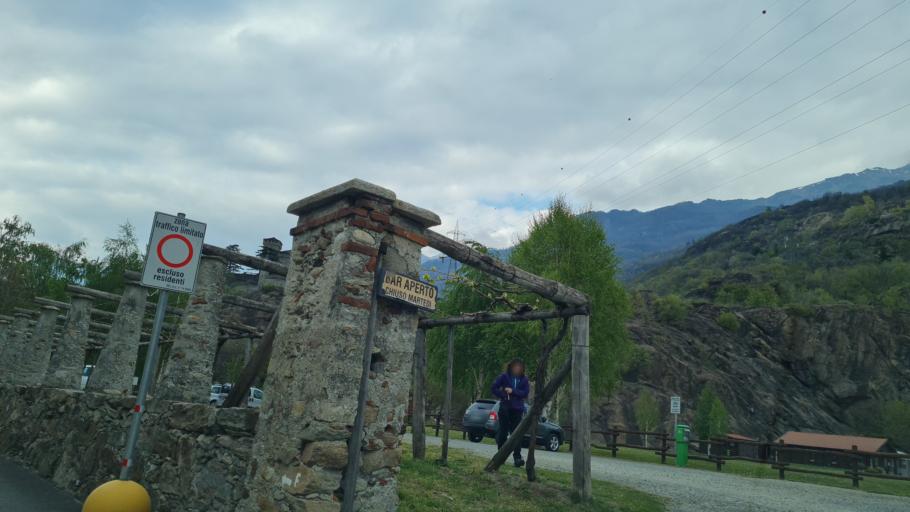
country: IT
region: Piedmont
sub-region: Provincia di Torino
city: Settimo Vittone
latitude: 45.5374
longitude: 7.8395
